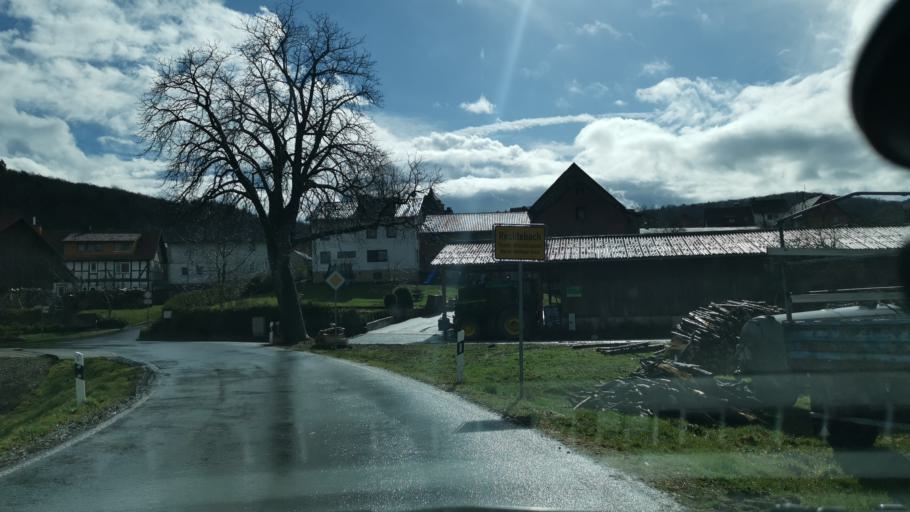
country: DE
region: Hesse
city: Waldkappel
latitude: 51.1174
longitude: 9.8721
